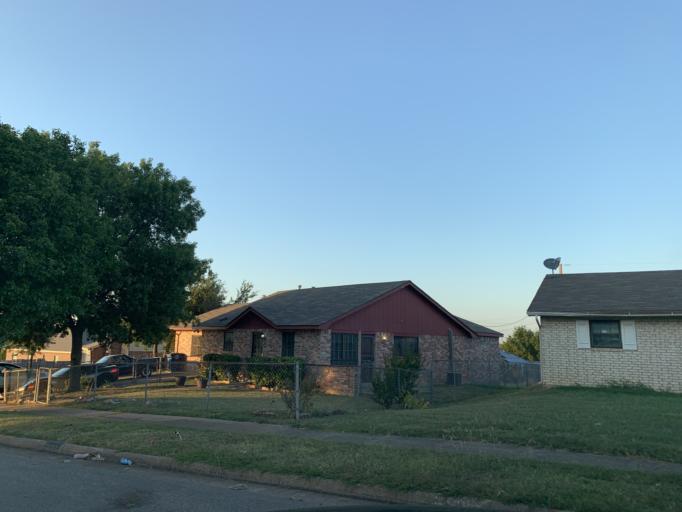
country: US
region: Texas
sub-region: Dallas County
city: Hutchins
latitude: 32.6681
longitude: -96.7963
